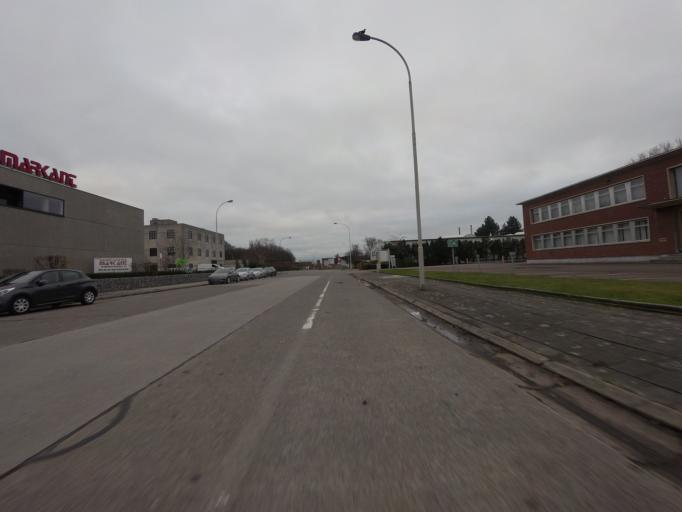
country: BE
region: Flanders
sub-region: Provincie Antwerpen
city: Aartselaar
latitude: 51.1541
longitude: 4.3750
